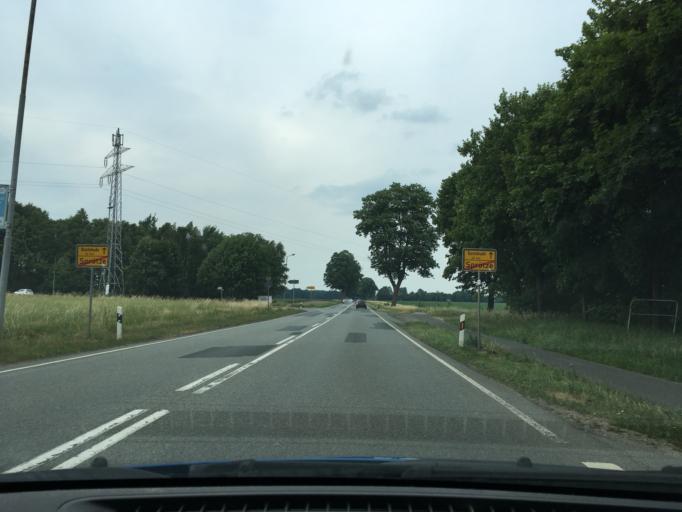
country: DE
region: Lower Saxony
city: Kakenstorf
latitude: 53.3129
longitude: 9.8048
